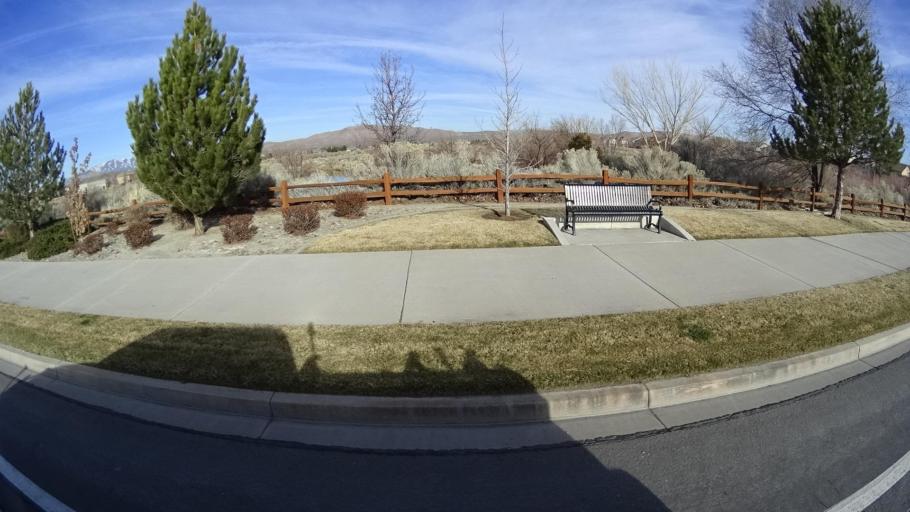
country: US
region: Nevada
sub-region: Washoe County
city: Spanish Springs
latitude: 39.6101
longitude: -119.6706
